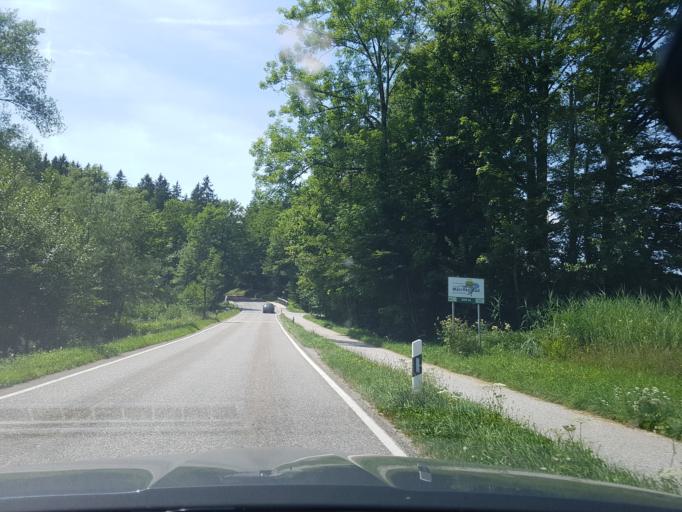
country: DE
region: Bavaria
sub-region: Upper Bavaria
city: Berchtesgaden
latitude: 47.6443
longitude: 12.9872
